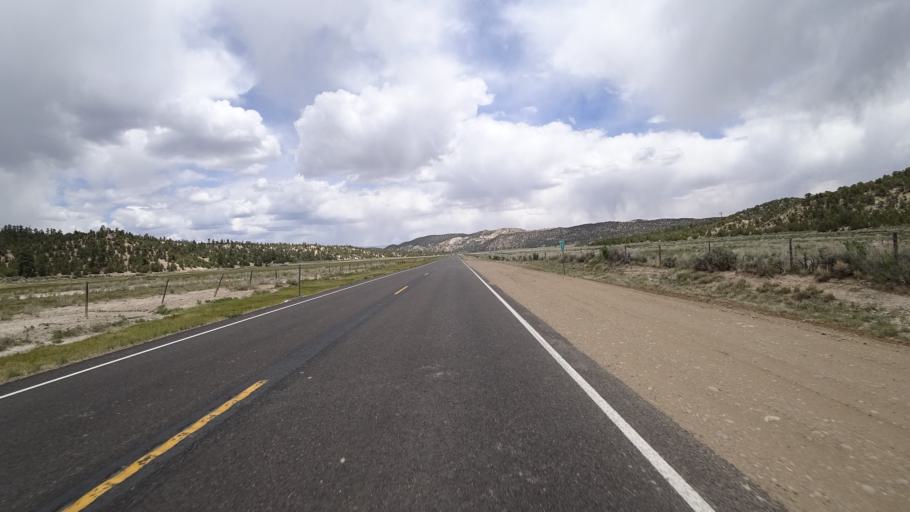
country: US
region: Utah
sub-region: Garfield County
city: Panguitch
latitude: 37.6849
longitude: -111.8094
